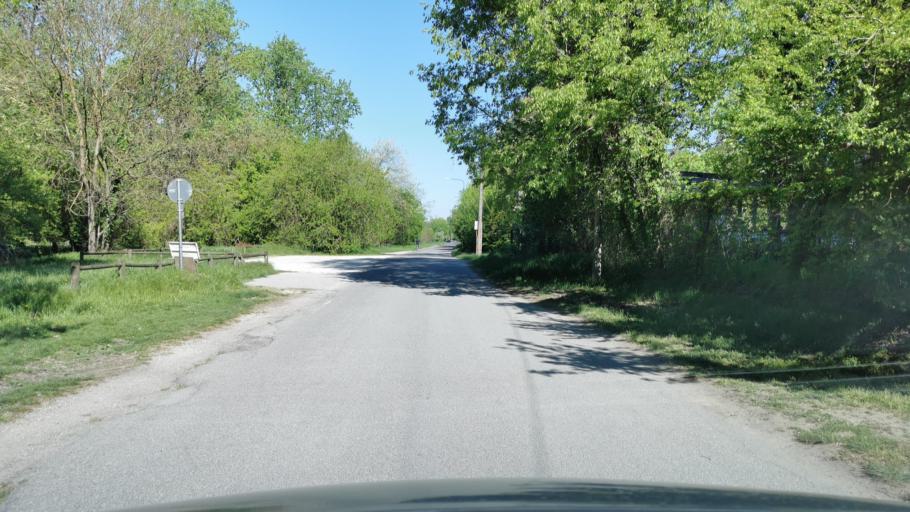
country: IT
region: Lombardy
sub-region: Provincia di Cremona
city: Cremona
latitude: 45.1195
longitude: 10.0093
